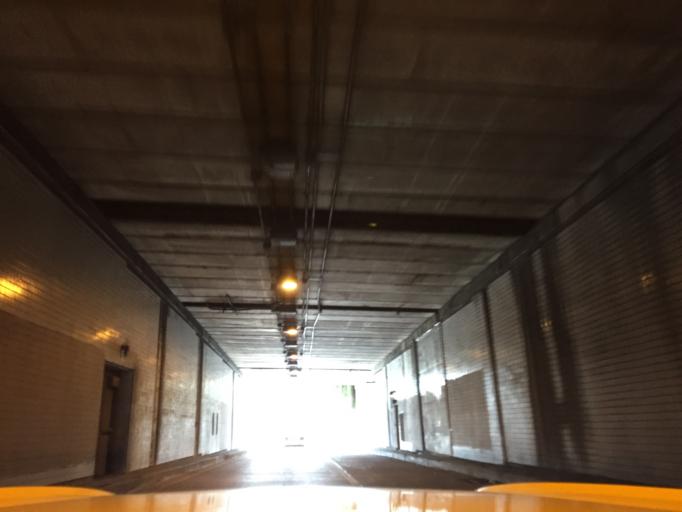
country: US
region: Pennsylvania
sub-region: Philadelphia County
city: Philadelphia
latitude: 39.9476
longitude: -75.1424
